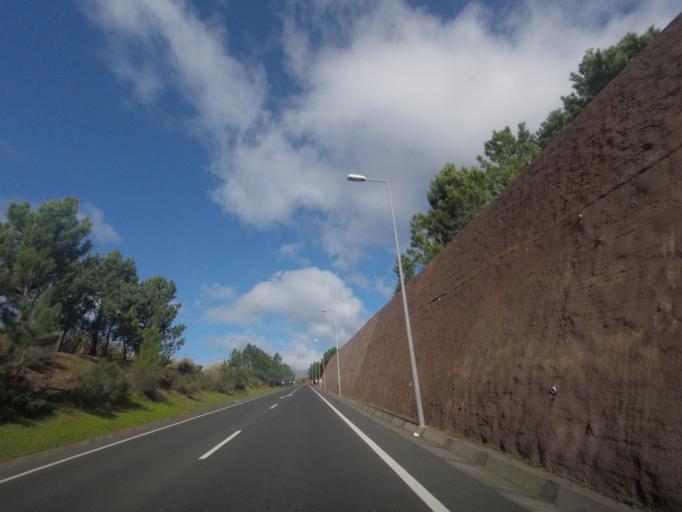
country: PT
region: Madeira
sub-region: Calheta
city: Estreito da Calheta
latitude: 32.7489
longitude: -17.2123
